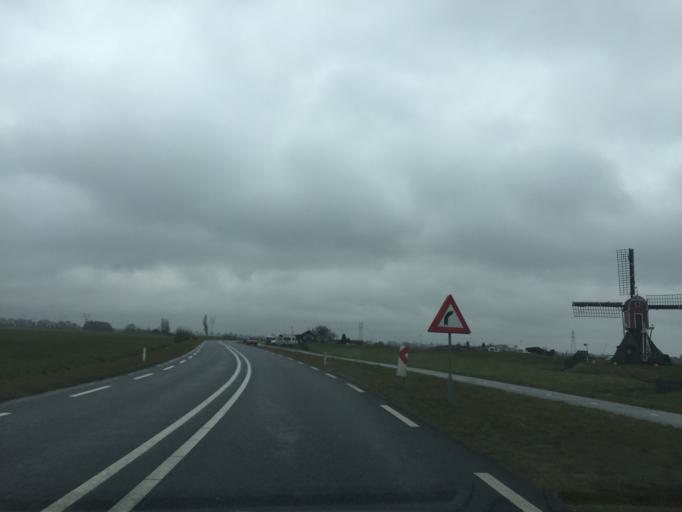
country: NL
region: South Holland
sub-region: Gemeente Leiderdorp
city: Leiderdorp
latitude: 52.1638
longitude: 4.5781
